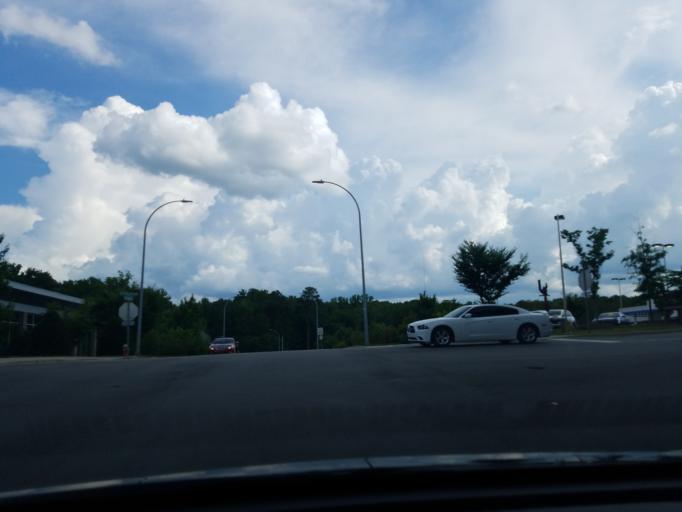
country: US
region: North Carolina
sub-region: Wake County
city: Apex
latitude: 35.7390
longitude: -78.8099
